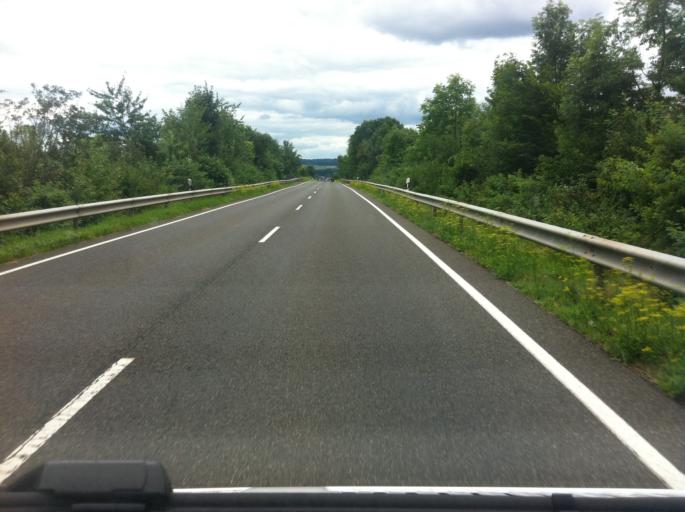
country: DE
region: North Rhine-Westphalia
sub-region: Regierungsbezirk Koln
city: Nettersheim
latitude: 50.5096
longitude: 6.6444
